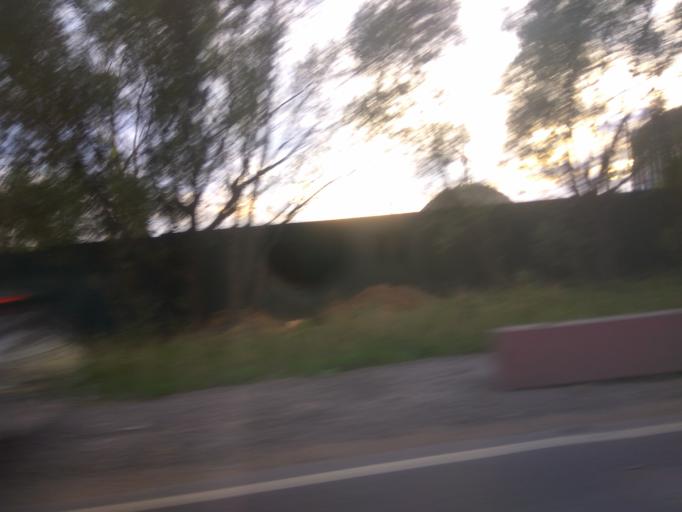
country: RU
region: Moscow
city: Solntsevo
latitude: 55.6320
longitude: 37.4203
